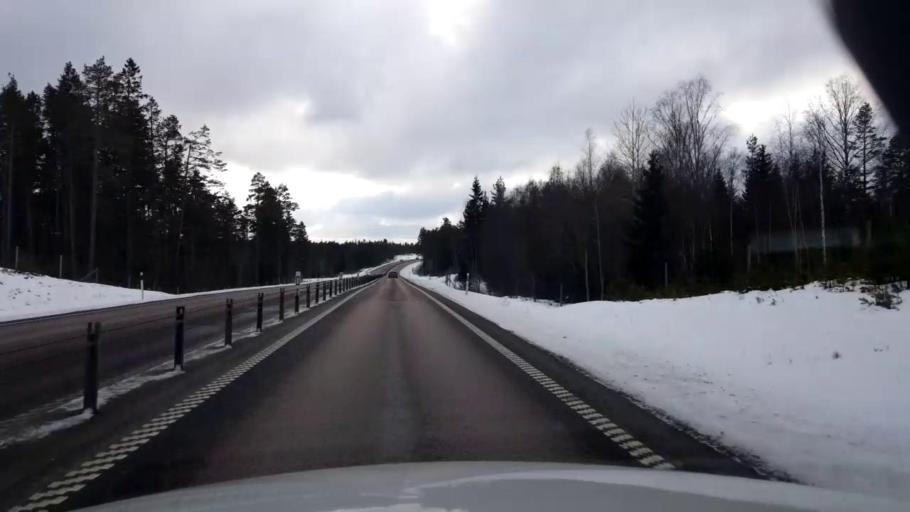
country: SE
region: Gaevleborg
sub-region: Hudiksvalls Kommun
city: Hudiksvall
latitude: 61.8168
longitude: 17.1897
